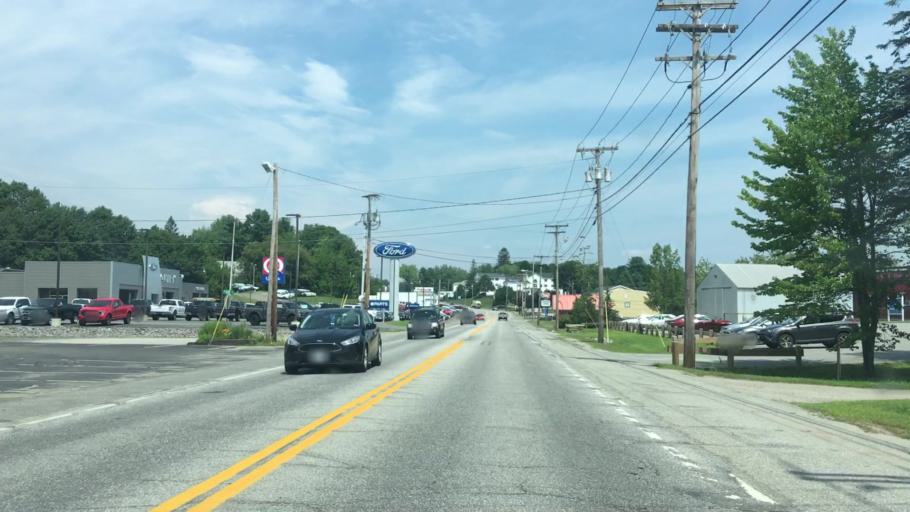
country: US
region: Maine
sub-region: Kennebec County
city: Hallowell
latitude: 44.2945
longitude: -69.7856
